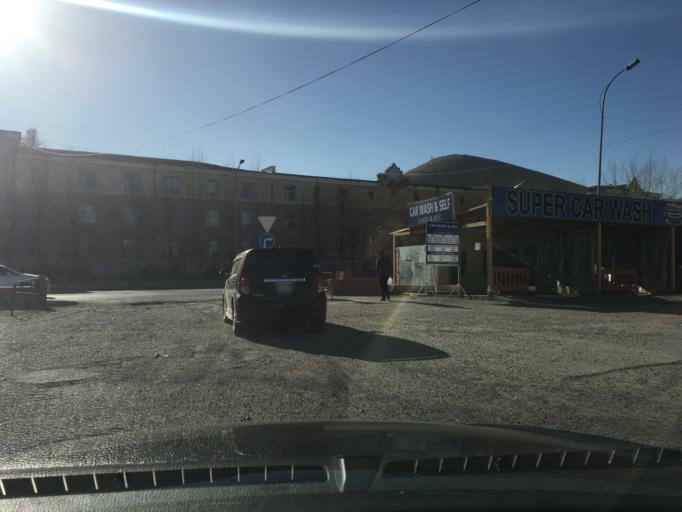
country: MN
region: Ulaanbaatar
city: Ulaanbaatar
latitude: 47.8879
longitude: 106.9099
